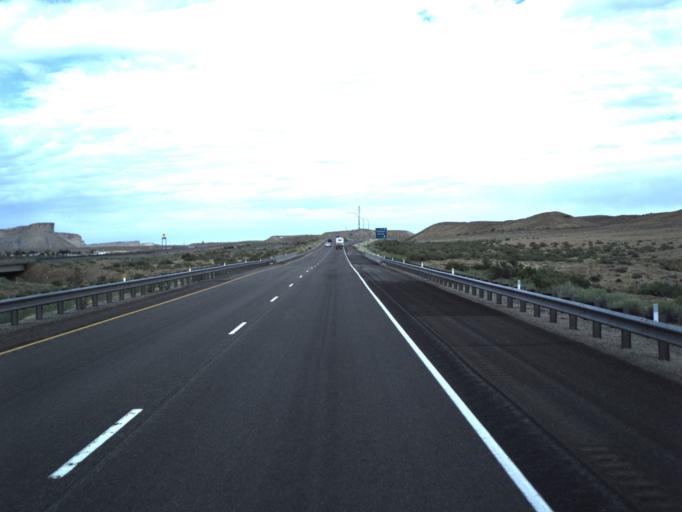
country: US
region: Utah
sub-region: Grand County
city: Moab
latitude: 38.9591
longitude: -109.7337
